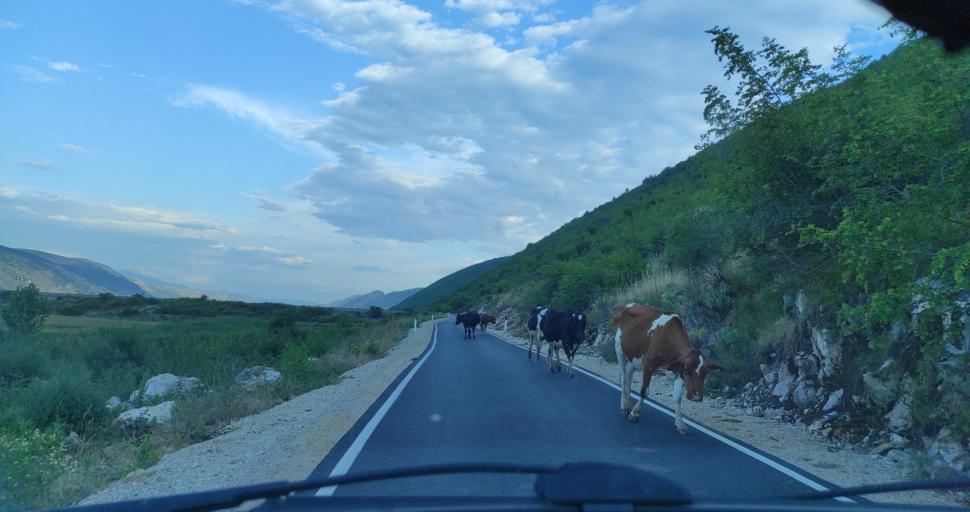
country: AL
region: Shkoder
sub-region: Rrethi i Shkodres
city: Velipoje
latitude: 41.9234
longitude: 19.4516
